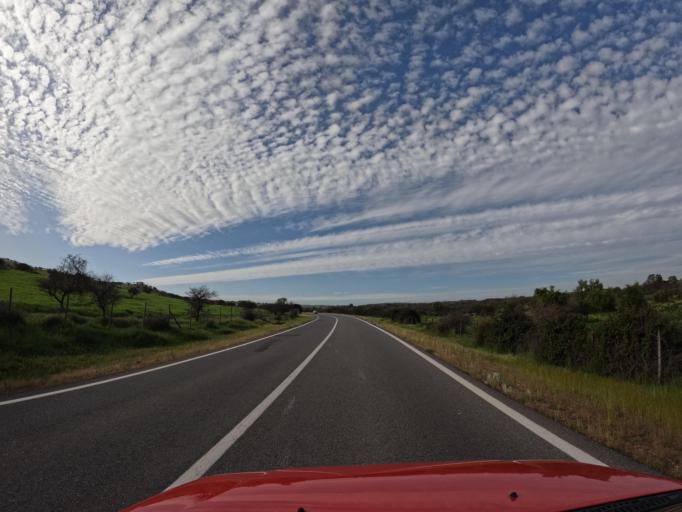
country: CL
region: O'Higgins
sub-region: Provincia de Colchagua
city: Santa Cruz
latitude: -34.2874
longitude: -71.7291
